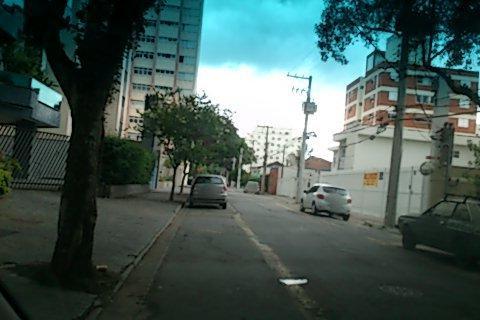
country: BR
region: Sao Paulo
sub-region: Sao Jose Dos Campos
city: Sao Jose dos Campos
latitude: -23.1990
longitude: -45.8943
